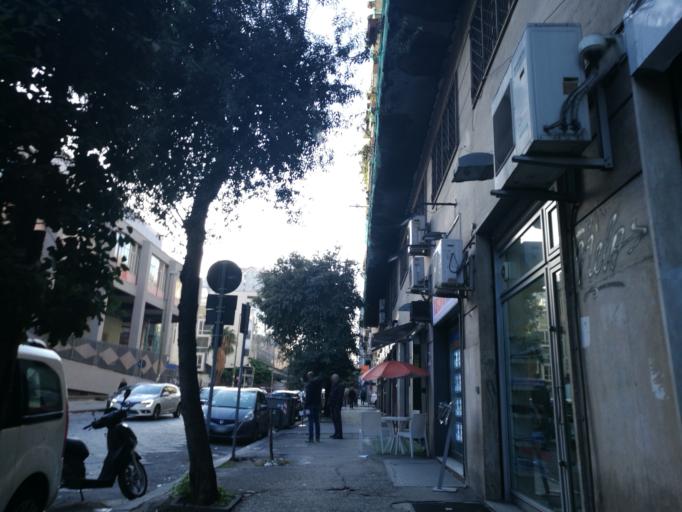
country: IT
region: Campania
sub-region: Provincia di Napoli
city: Napoli
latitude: 40.8547
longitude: 14.2759
